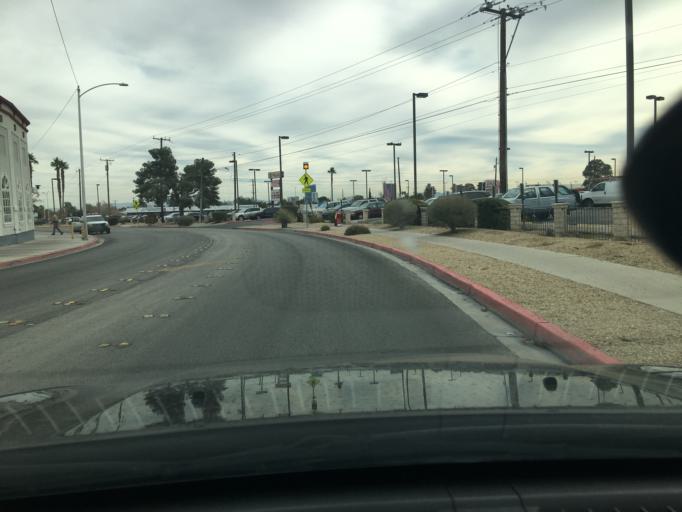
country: US
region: Nevada
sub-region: Clark County
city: Spring Valley
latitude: 36.1630
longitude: -115.2080
